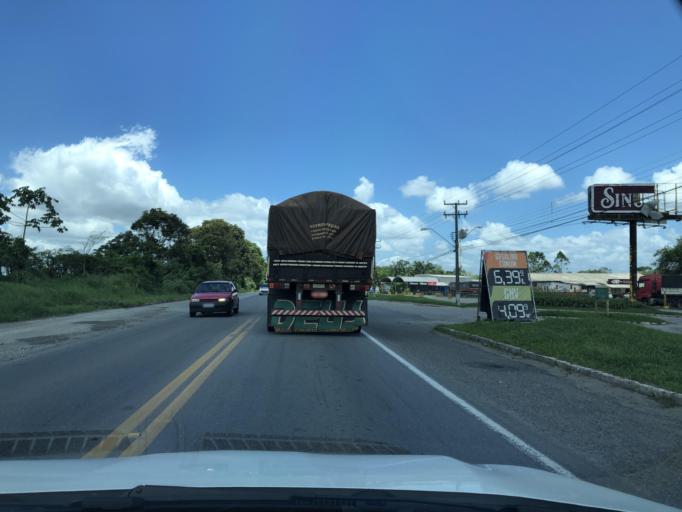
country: BR
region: Santa Catarina
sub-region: Sao Francisco Do Sul
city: Sao Francisco do Sul
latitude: -26.3712
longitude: -48.7065
